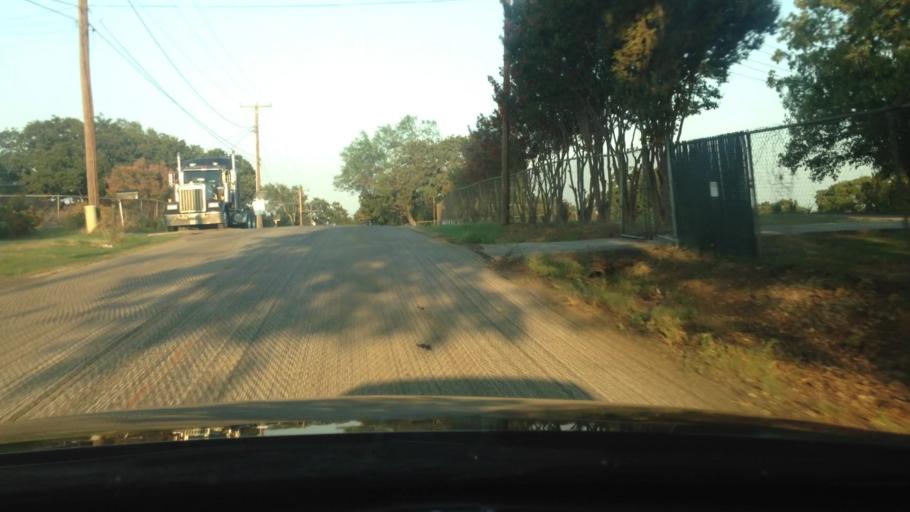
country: US
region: Texas
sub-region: Tarrant County
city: Rendon
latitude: 32.6016
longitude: -97.2341
